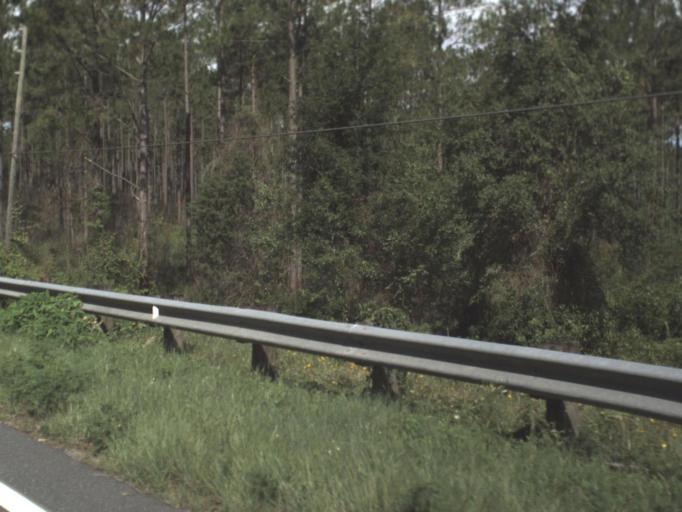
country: US
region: Florida
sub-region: Madison County
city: Madison
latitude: 30.4884
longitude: -83.3878
